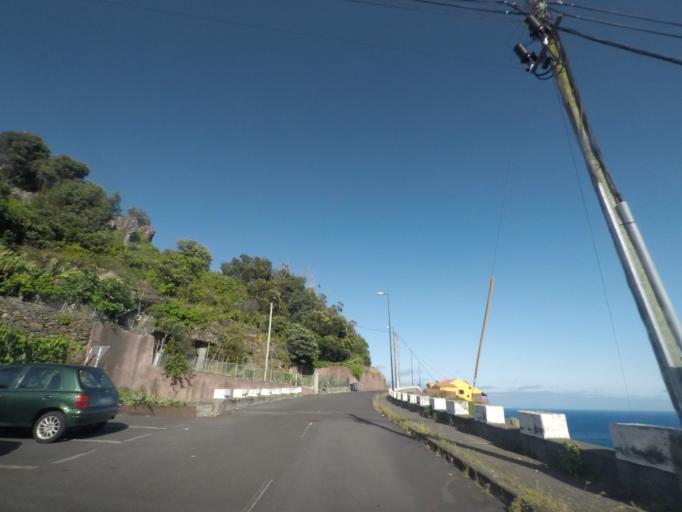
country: PT
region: Madeira
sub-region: Santa Cruz
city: Santa Cruz
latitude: 32.6913
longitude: -16.7949
